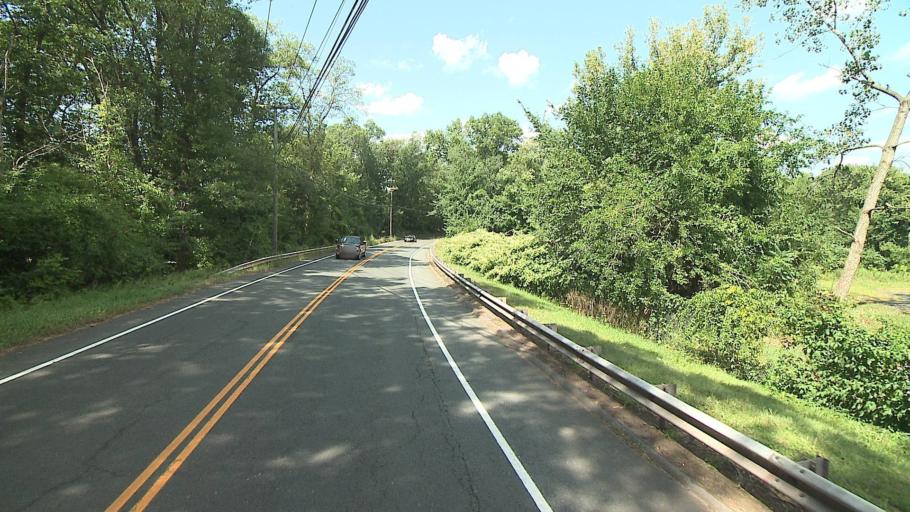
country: US
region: Connecticut
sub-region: Hartford County
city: Broad Brook
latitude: 41.9308
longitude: -72.5109
